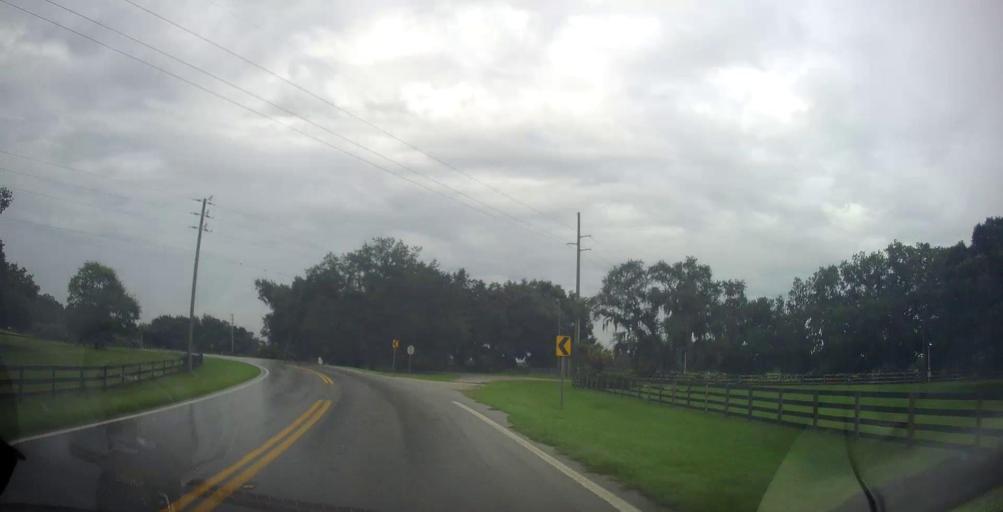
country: US
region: Florida
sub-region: Marion County
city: Citra
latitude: 29.3313
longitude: -82.2058
